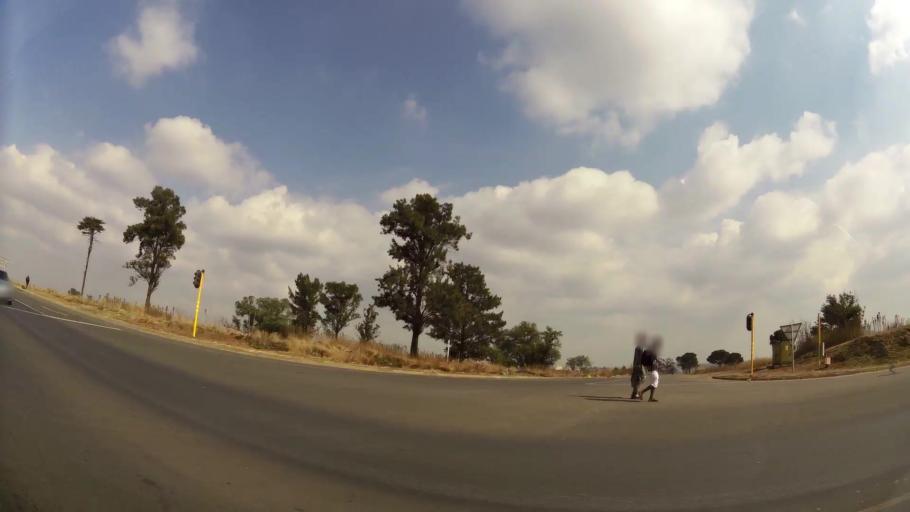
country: ZA
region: Gauteng
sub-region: Ekurhuleni Metropolitan Municipality
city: Brakpan
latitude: -26.1745
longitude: 28.3977
